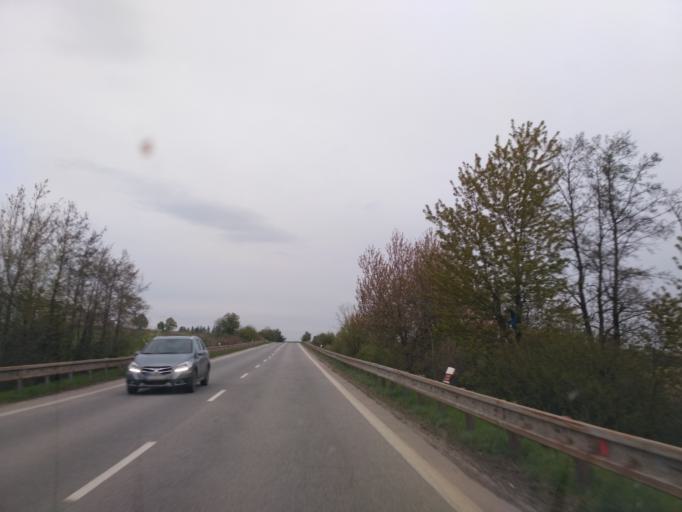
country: SK
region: Kosicky
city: Moldava nad Bodvou
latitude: 48.6864
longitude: 21.0636
